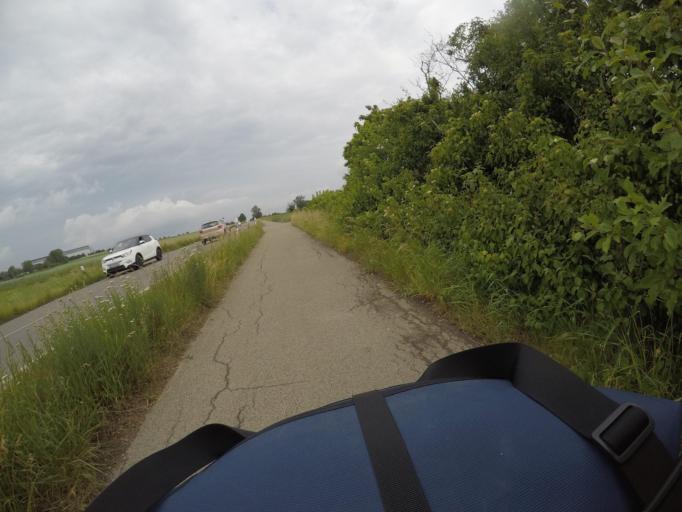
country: DE
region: Baden-Wuerttemberg
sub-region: Regierungsbezirk Stuttgart
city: Gerlingen
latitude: 48.8106
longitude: 9.0695
